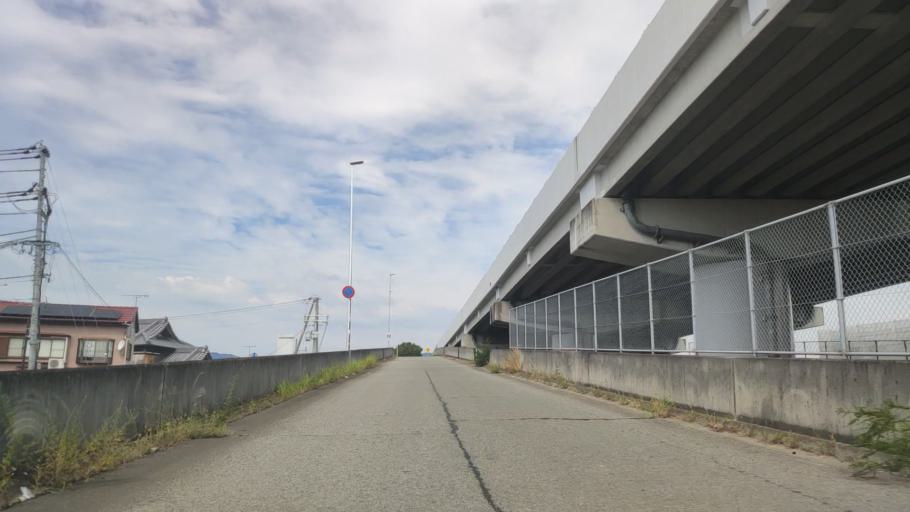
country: JP
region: Wakayama
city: Wakayama-shi
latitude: 34.2456
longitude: 135.2180
